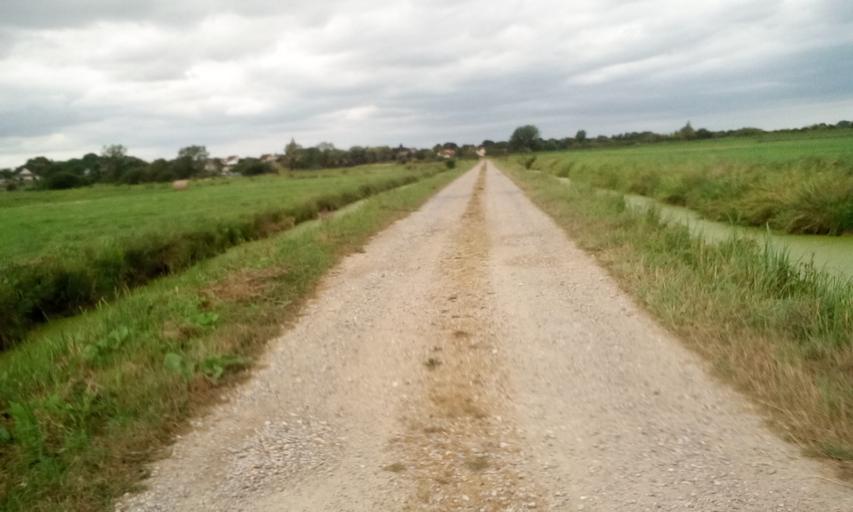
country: FR
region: Lower Normandy
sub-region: Departement du Calvados
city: Troarn
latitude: 49.1941
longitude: -0.1684
